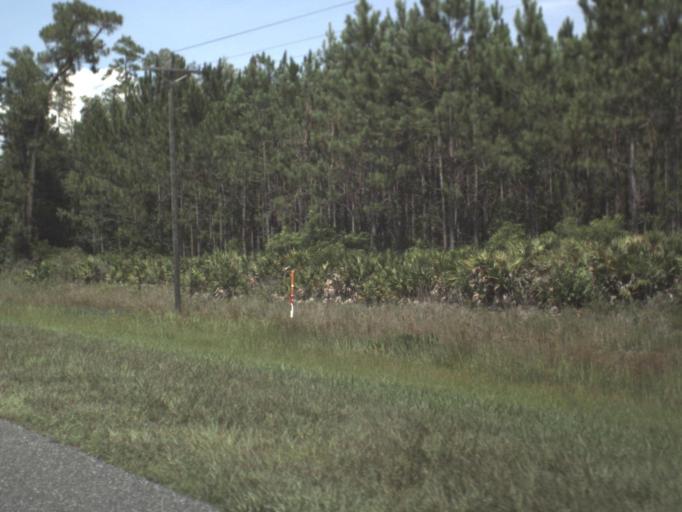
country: US
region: Florida
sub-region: Levy County
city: Inglis
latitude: 29.0719
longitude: -82.6449
